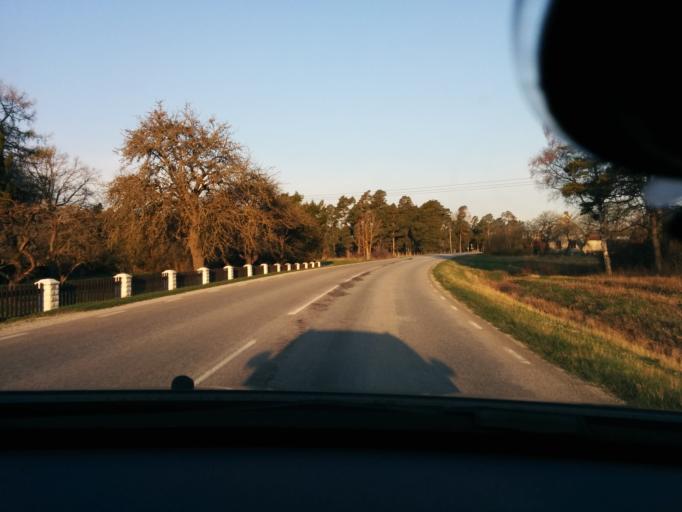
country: SE
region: Gotland
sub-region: Gotland
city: Slite
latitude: 57.6286
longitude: 18.5787
